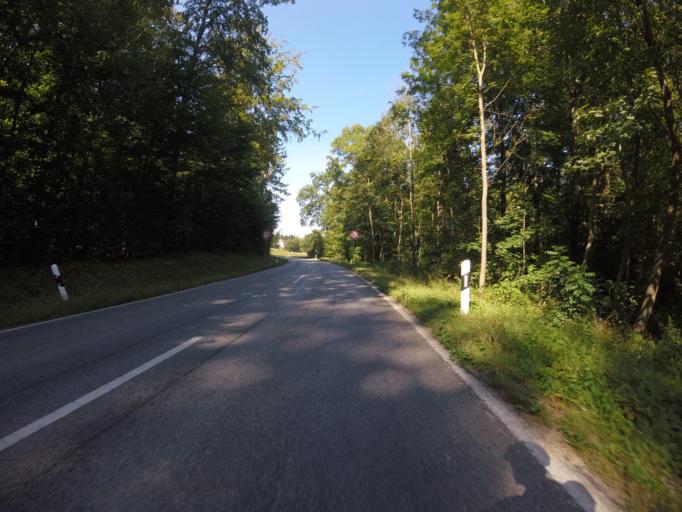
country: DE
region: Baden-Wuerttemberg
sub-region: Regierungsbezirk Stuttgart
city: Ilsfeld
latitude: 49.0327
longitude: 9.2430
